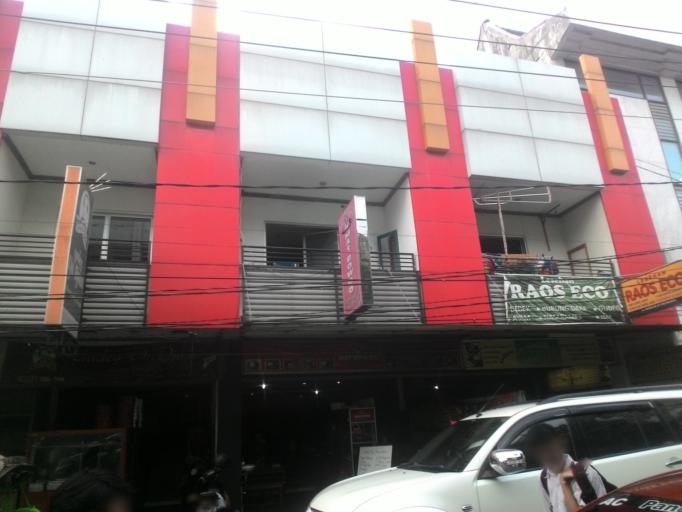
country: ID
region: Daerah Istimewa Yogyakarta
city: Yogyakarta
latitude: -7.7940
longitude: 110.3653
